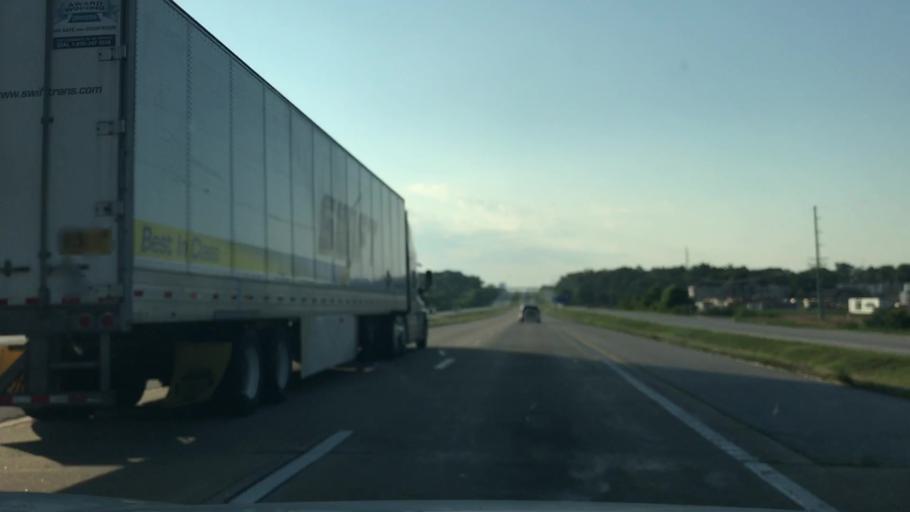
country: US
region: Missouri
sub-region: Saint Charles County
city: Dardenne Prairie
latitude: 38.7352
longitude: -90.7402
